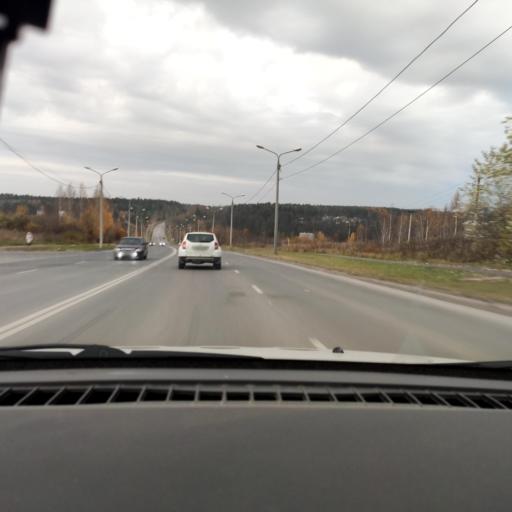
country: RU
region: Perm
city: Perm
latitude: 58.0667
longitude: 56.3658
